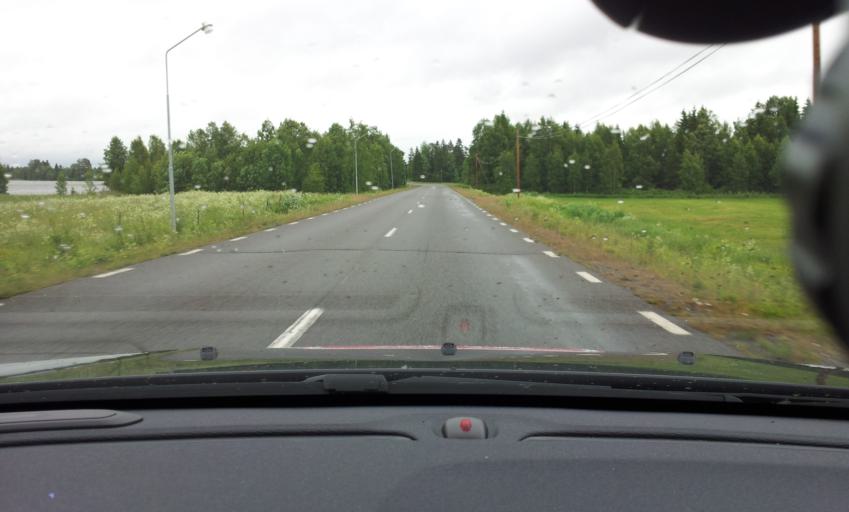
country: SE
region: Jaemtland
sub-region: OEstersunds Kommun
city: Lit
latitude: 63.6718
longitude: 15.0805
